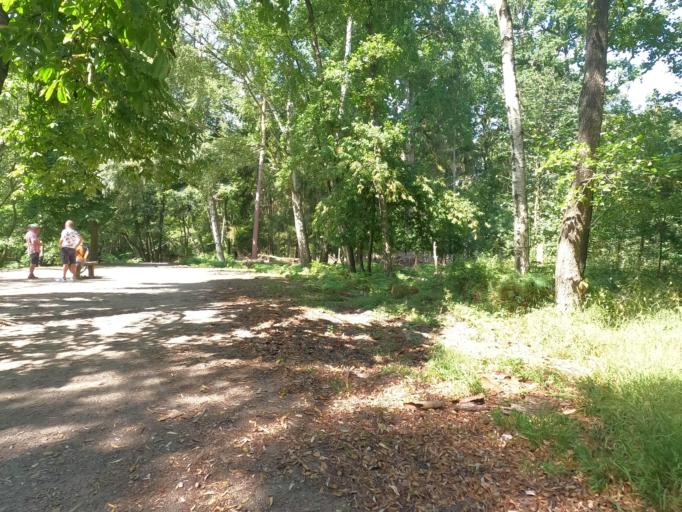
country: DE
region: Hesse
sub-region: Regierungsbezirk Darmstadt
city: Neu Isenburg
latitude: 50.0664
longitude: 8.7083
